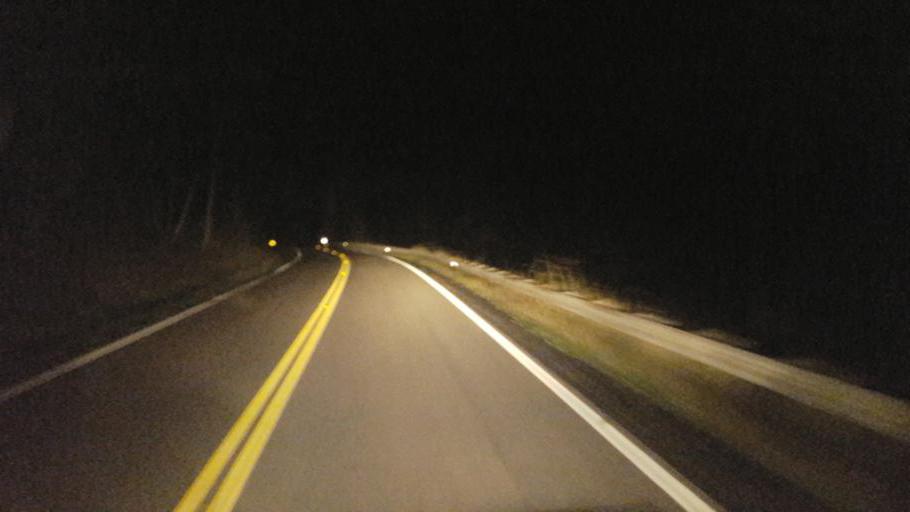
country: US
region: Ohio
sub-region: Harrison County
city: Cadiz
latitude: 40.3462
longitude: -81.1337
